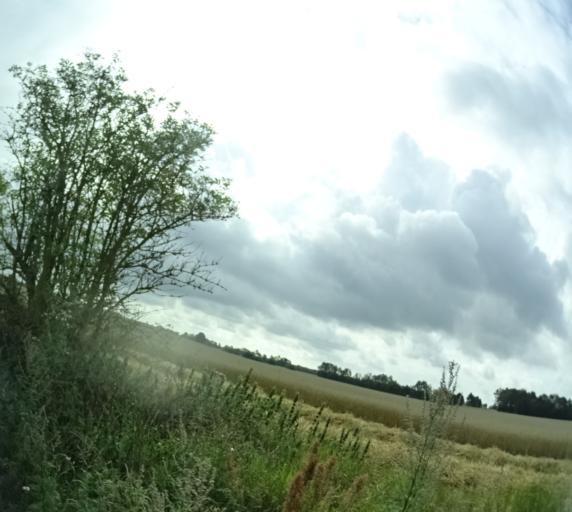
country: DK
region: Central Jutland
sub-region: Syddjurs Kommune
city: Ryomgard
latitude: 56.3505
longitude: 10.5033
